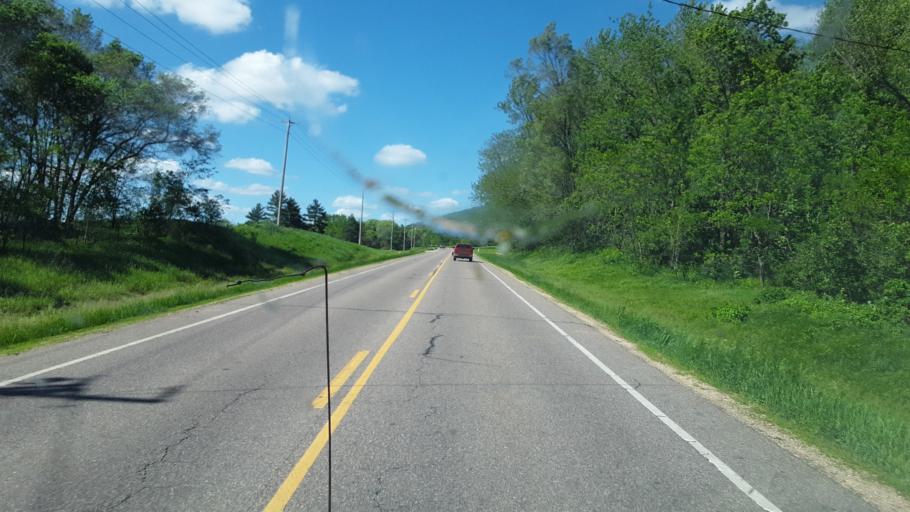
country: US
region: Wisconsin
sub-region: Juneau County
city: Mauston
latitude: 43.7667
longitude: -90.0779
